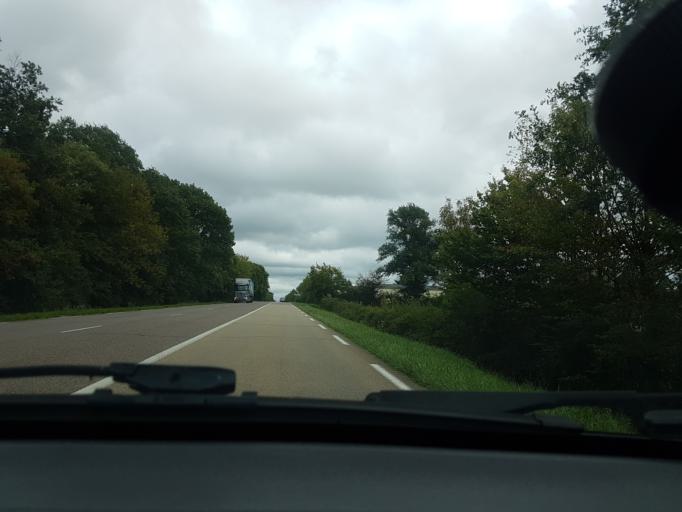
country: FR
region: Bourgogne
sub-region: Departement de la Cote-d'Or
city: Saulieu
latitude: 47.4290
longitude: 4.1026
